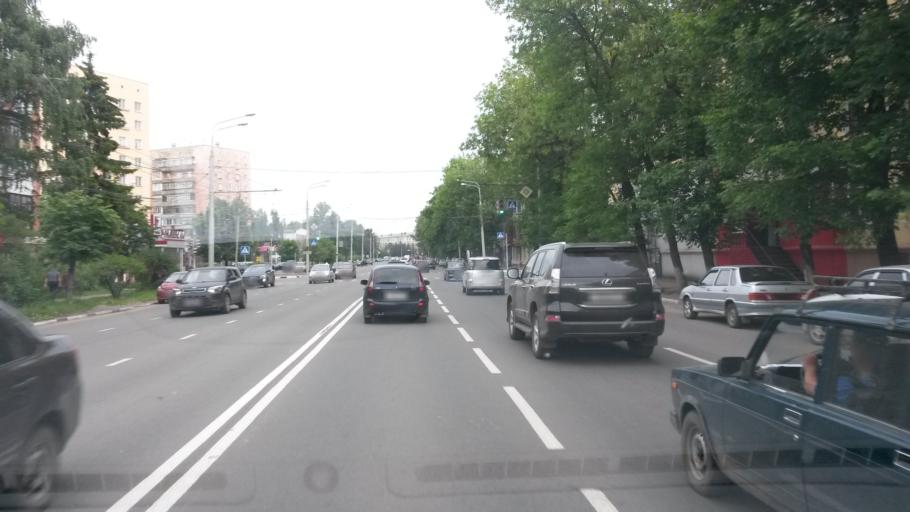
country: RU
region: Jaroslavl
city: Yaroslavl
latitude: 57.6286
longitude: 39.8583
